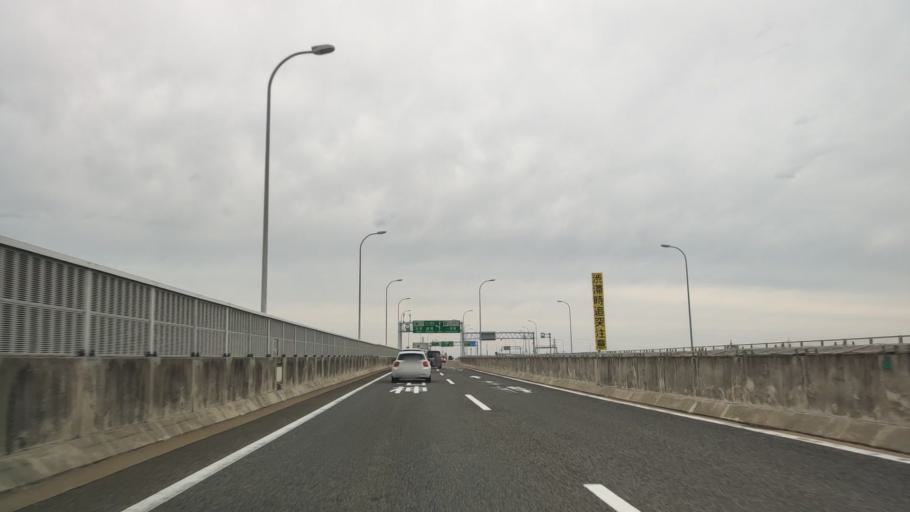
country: JP
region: Aichi
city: Iwakura
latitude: 35.2677
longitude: 136.8350
